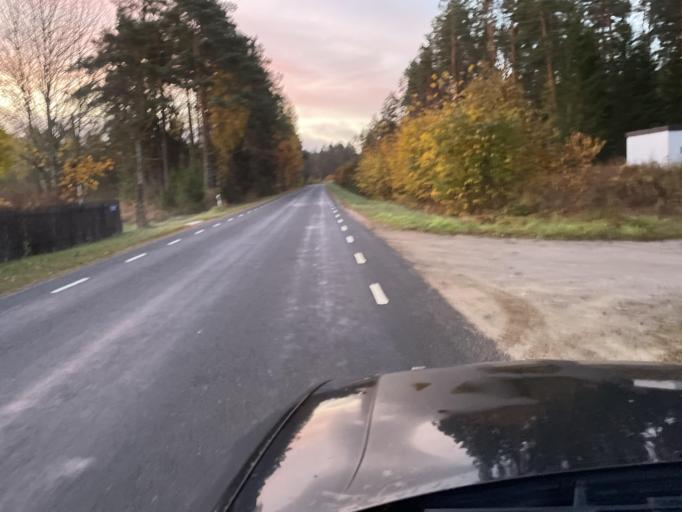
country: EE
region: Harju
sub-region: Nissi vald
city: Riisipere
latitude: 59.2540
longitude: 24.2300
